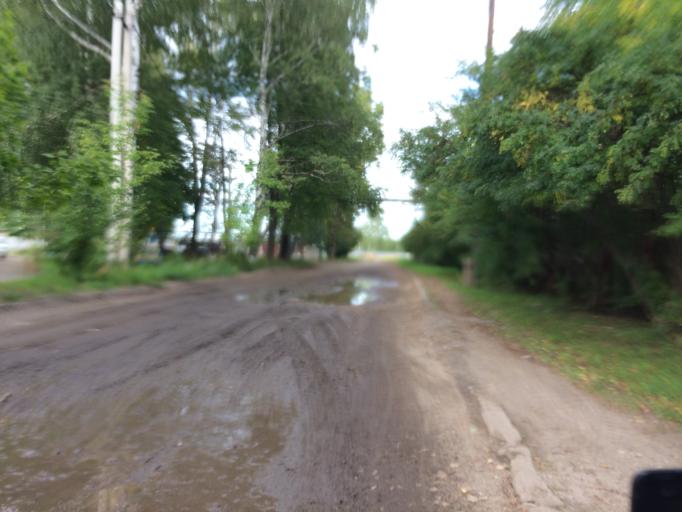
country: RU
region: Mariy-El
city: Yoshkar-Ola
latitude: 56.6589
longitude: 48.0094
